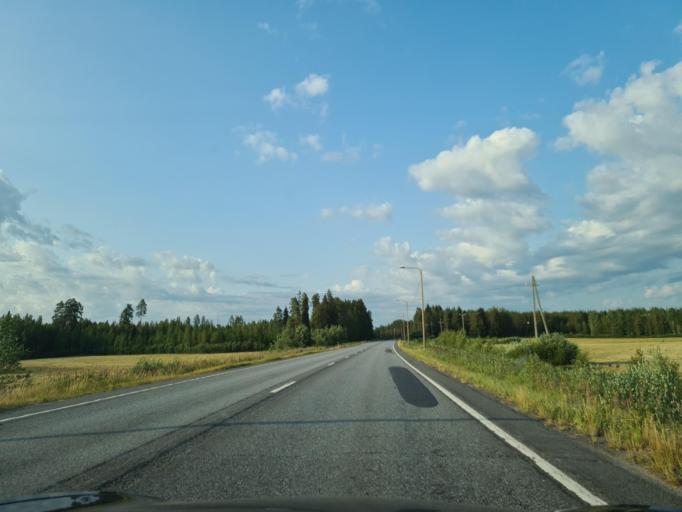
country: FI
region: Southern Ostrobothnia
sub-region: Seinaejoki
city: Kauhava
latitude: 63.0692
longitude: 23.0480
